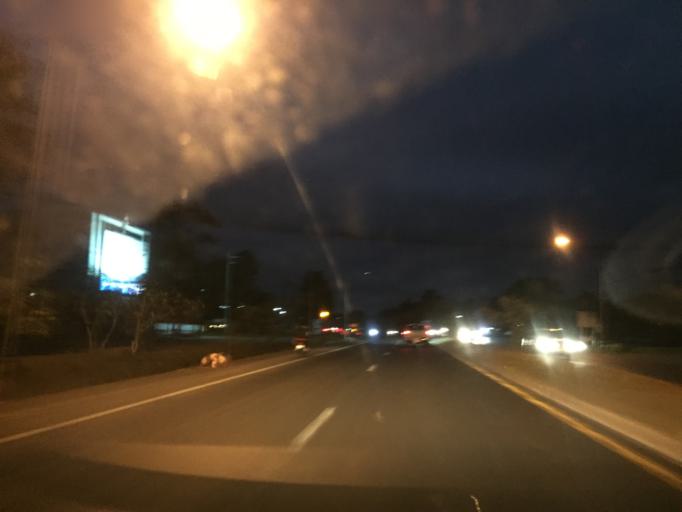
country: TH
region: Changwat Nong Bua Lamphu
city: Na Klang
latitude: 17.2963
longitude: 102.2132
